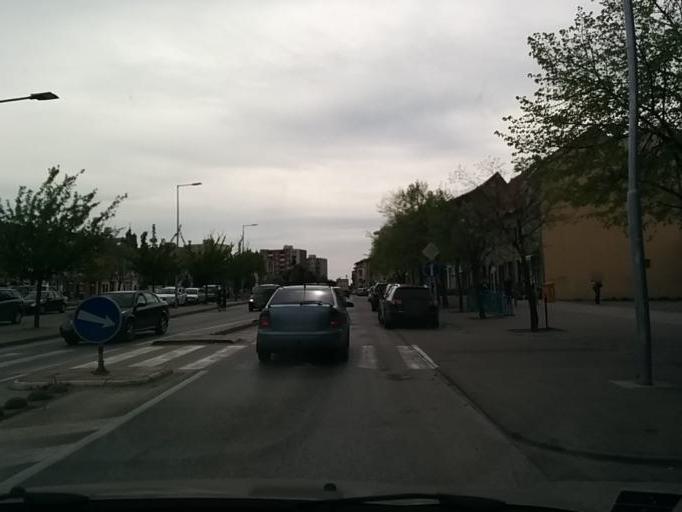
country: SK
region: Bratislavsky
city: Senec
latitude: 48.2211
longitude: 17.3990
